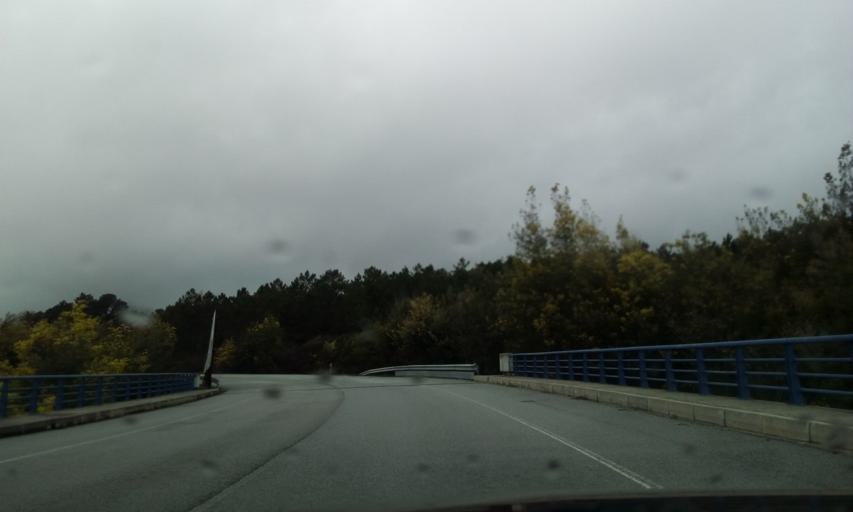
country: PT
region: Guarda
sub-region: Fornos de Algodres
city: Fornos de Algodres
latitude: 40.6228
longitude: -7.5983
